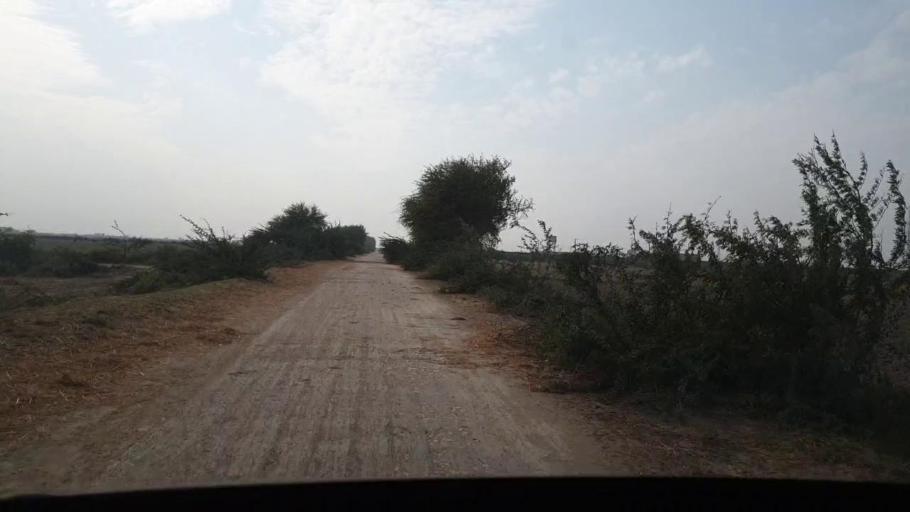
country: PK
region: Sindh
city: Chuhar Jamali
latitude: 24.3197
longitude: 68.0584
